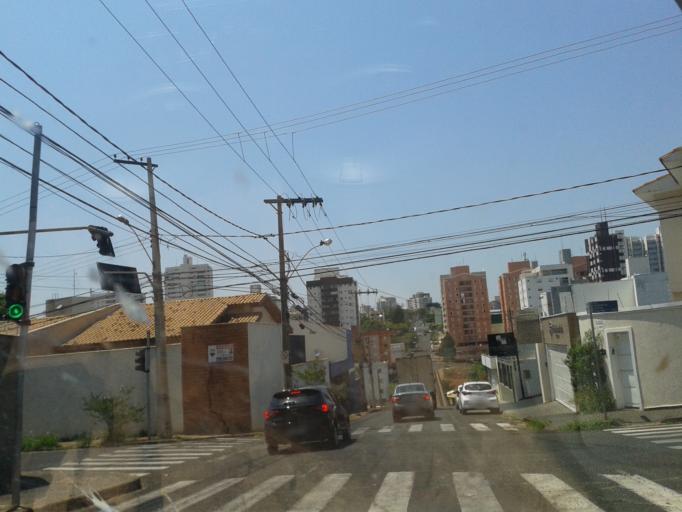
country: BR
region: Minas Gerais
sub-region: Uberlandia
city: Uberlandia
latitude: -18.9181
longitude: -48.2681
